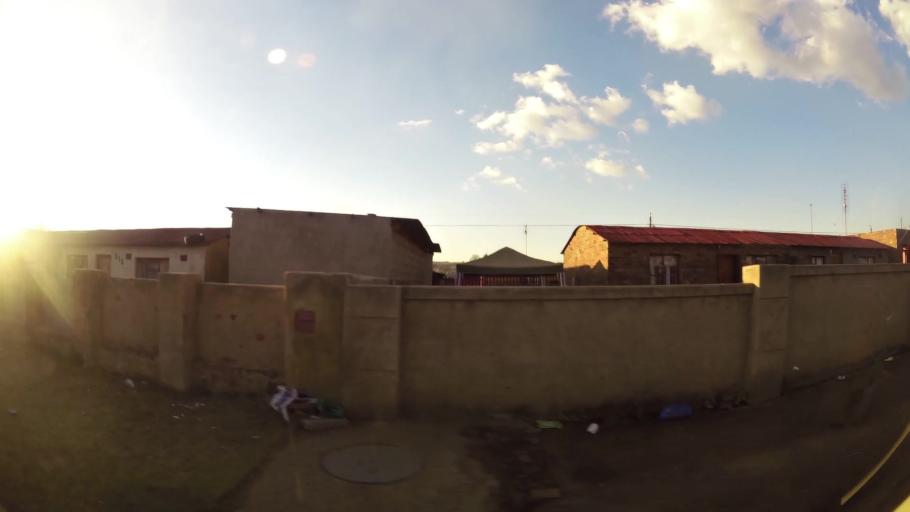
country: ZA
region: Mpumalanga
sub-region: Nkangala District Municipality
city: Witbank
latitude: -25.8769
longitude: 29.1920
